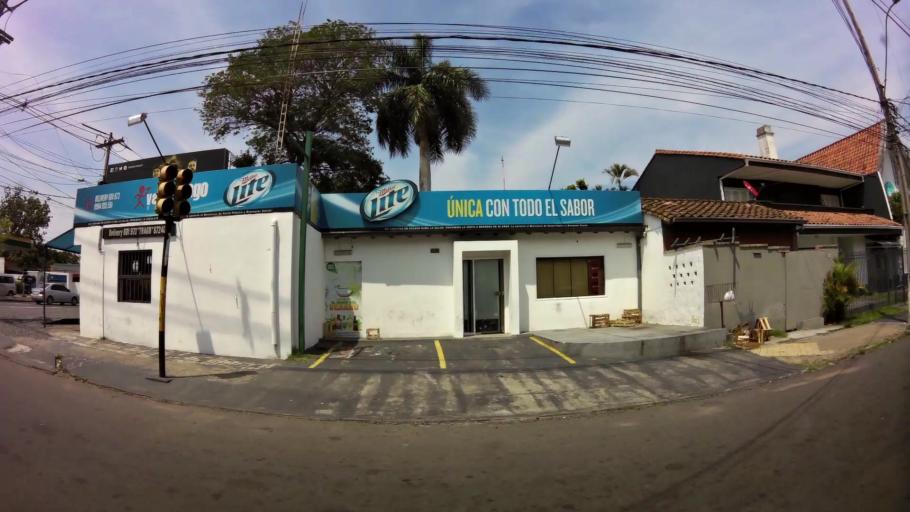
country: PY
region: Asuncion
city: Asuncion
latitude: -25.2846
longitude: -57.5885
